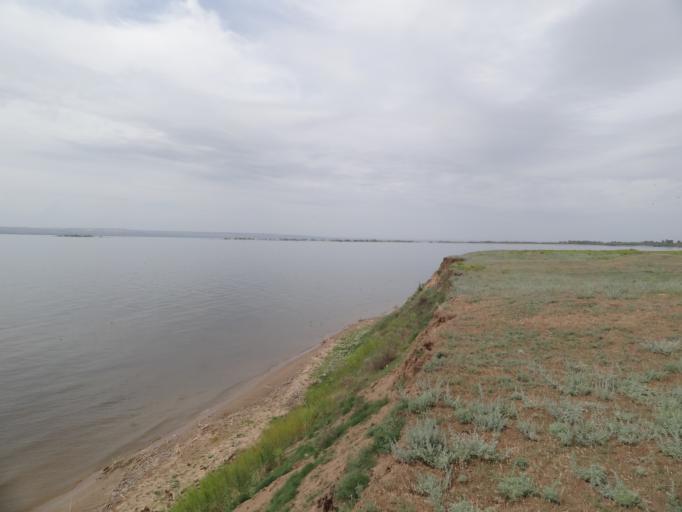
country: RU
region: Saratov
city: Privolzhskiy
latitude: 51.1993
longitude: 45.9079
